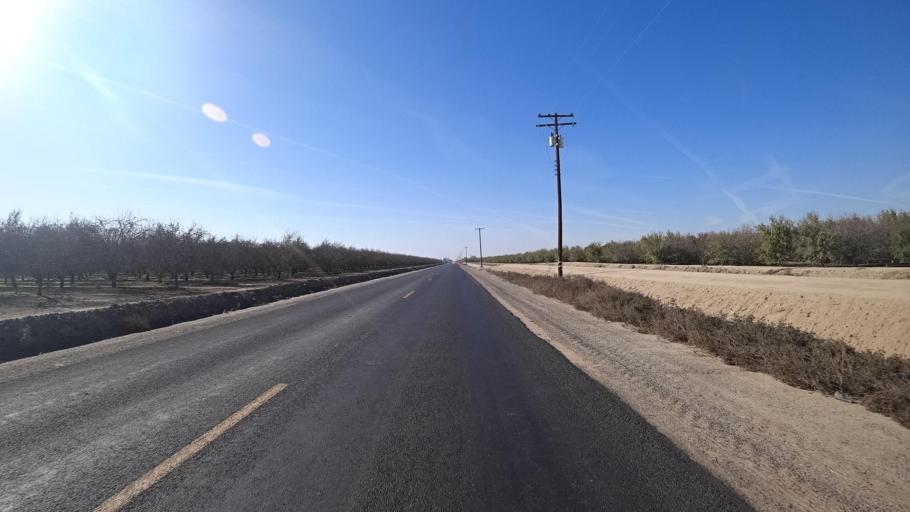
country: US
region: California
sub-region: Kern County
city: Wasco
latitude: 35.6452
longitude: -119.3068
